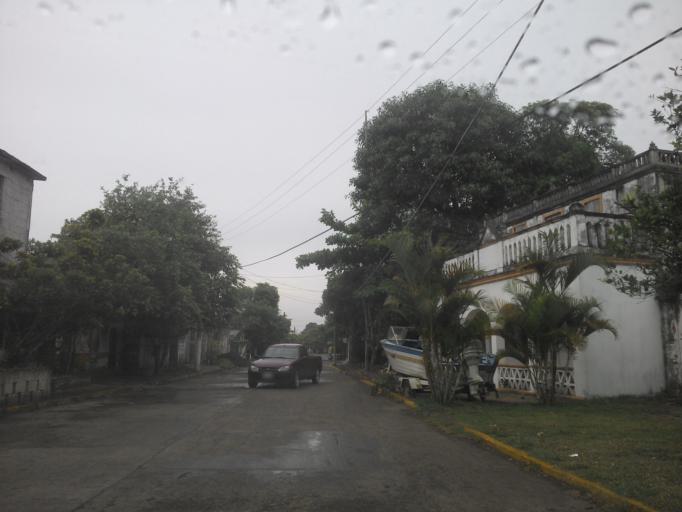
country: MX
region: Veracruz
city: Nautla
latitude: 20.2108
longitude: -96.7757
